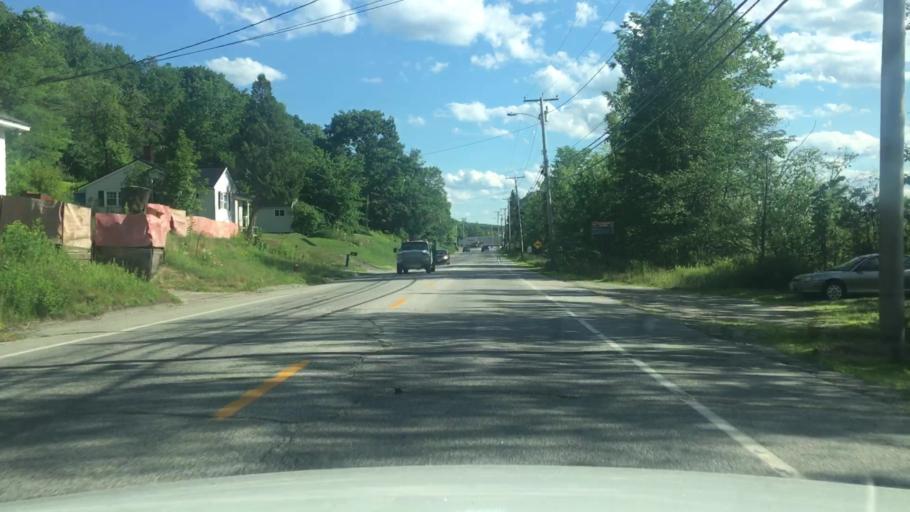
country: US
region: Maine
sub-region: Franklin County
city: Wilton
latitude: 44.5506
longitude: -70.2373
